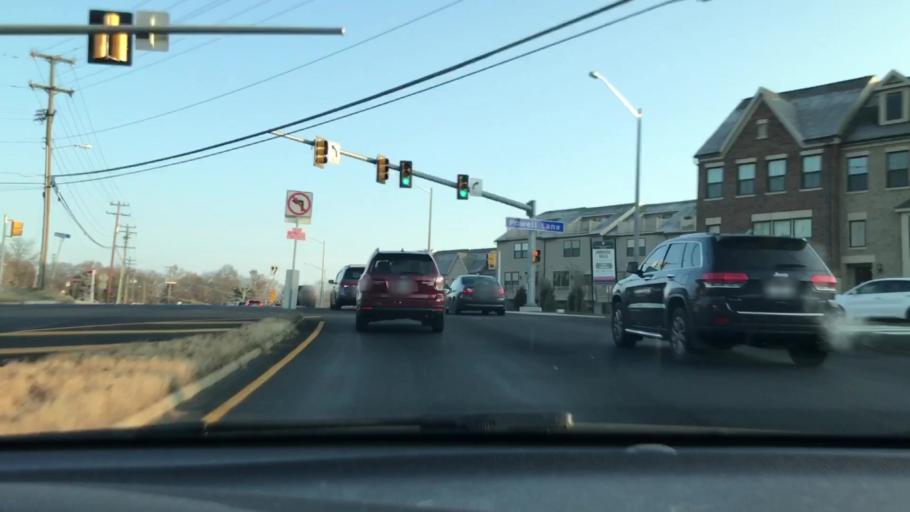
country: US
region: Virginia
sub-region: Fairfax County
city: Baileys Crossroads
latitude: 38.8435
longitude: -77.1419
